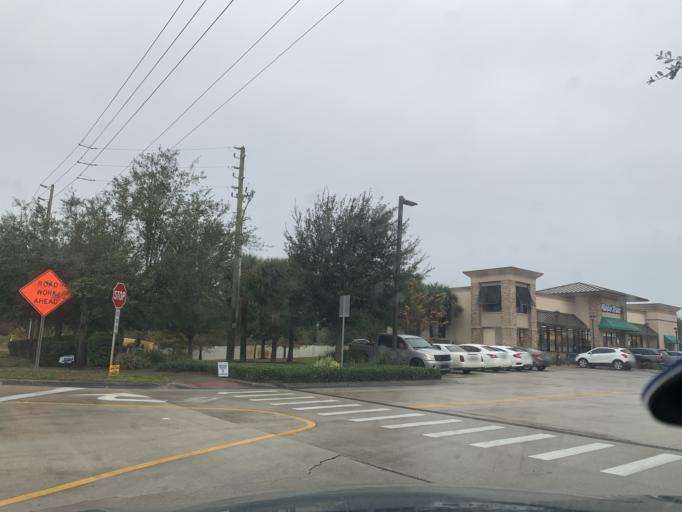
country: US
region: Florida
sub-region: Pasco County
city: Shady Hills
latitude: 28.3302
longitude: -82.5591
